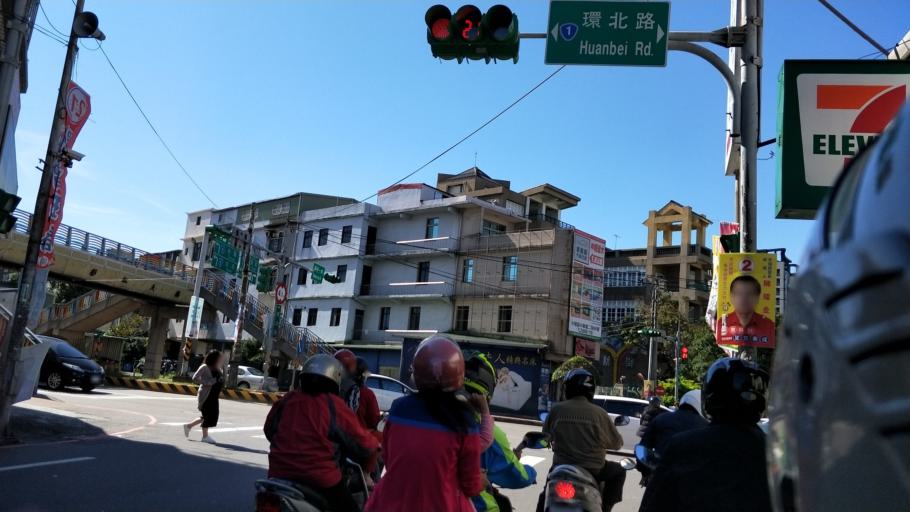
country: TW
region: Taiwan
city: Taoyuan City
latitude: 24.9646
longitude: 121.2292
